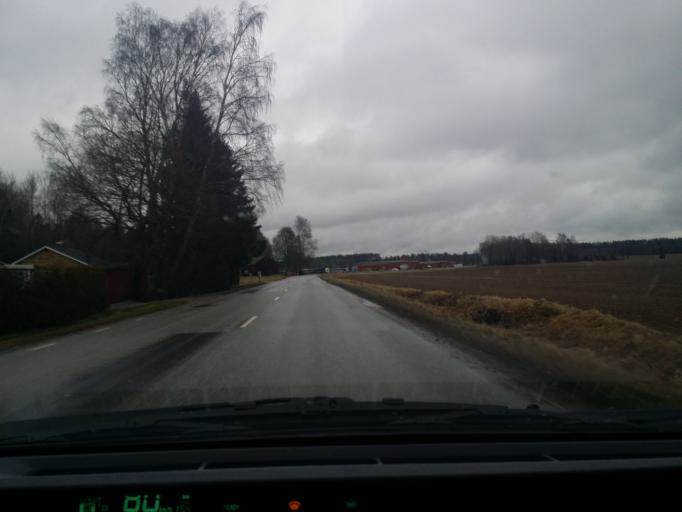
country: SE
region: Vaestmanland
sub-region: Vasteras
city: Skultuna
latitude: 59.8037
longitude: 16.5241
